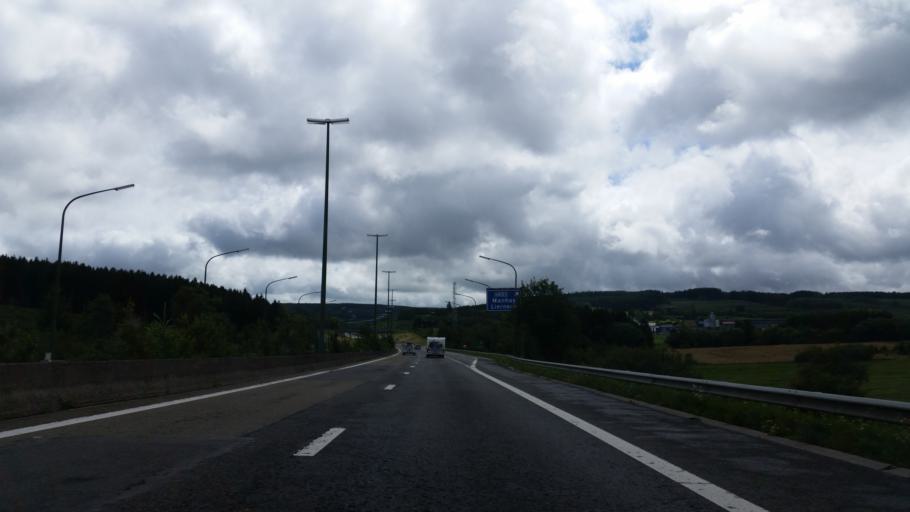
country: BE
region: Wallonia
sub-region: Province du Luxembourg
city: Manhay
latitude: 50.3126
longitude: 5.7096
